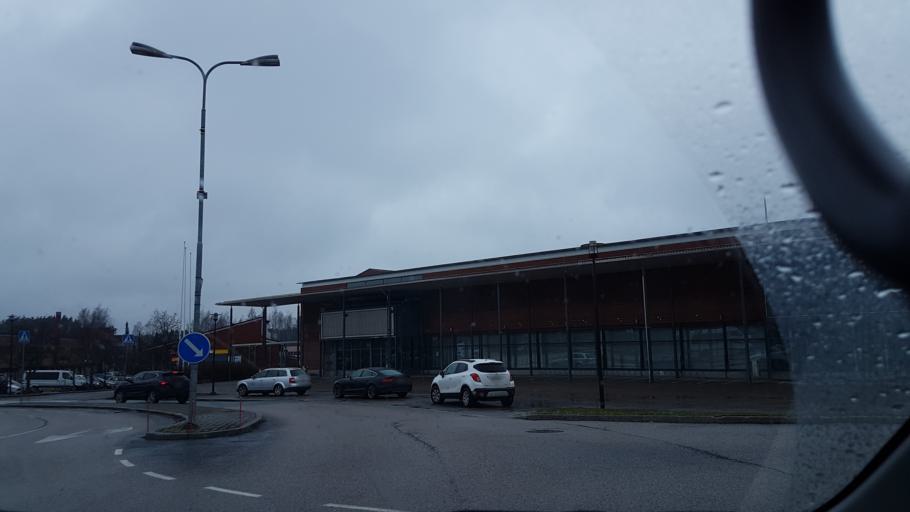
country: FI
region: Uusimaa
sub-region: Helsinki
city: Tuusula
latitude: 60.4023
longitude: 25.0290
